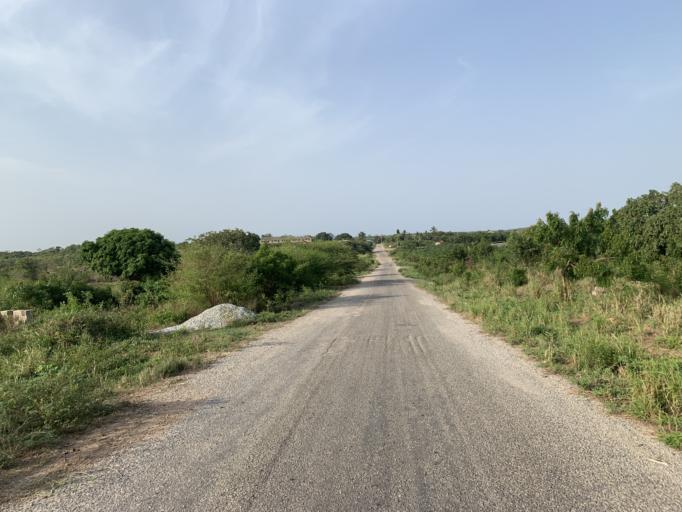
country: GH
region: Central
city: Winneba
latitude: 5.3875
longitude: -0.6041
